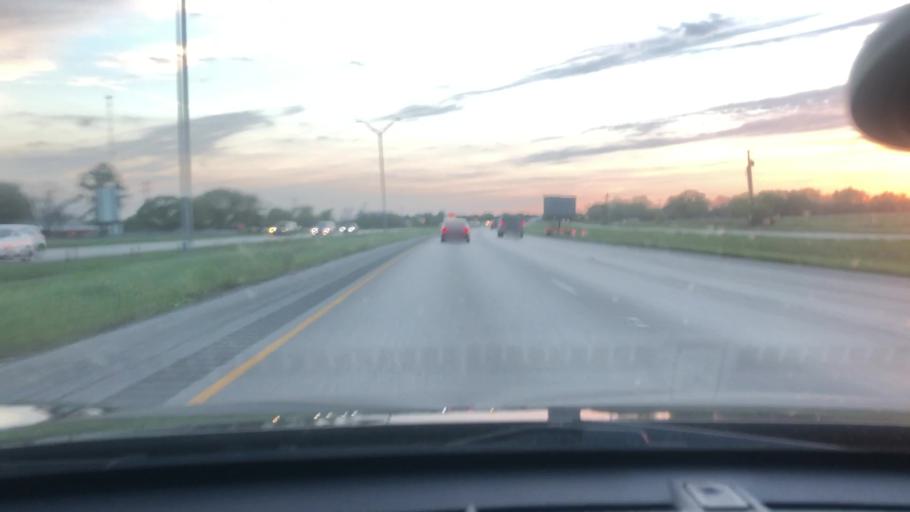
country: US
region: Texas
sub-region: Jackson County
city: Edna
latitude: 28.9638
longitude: -96.6761
